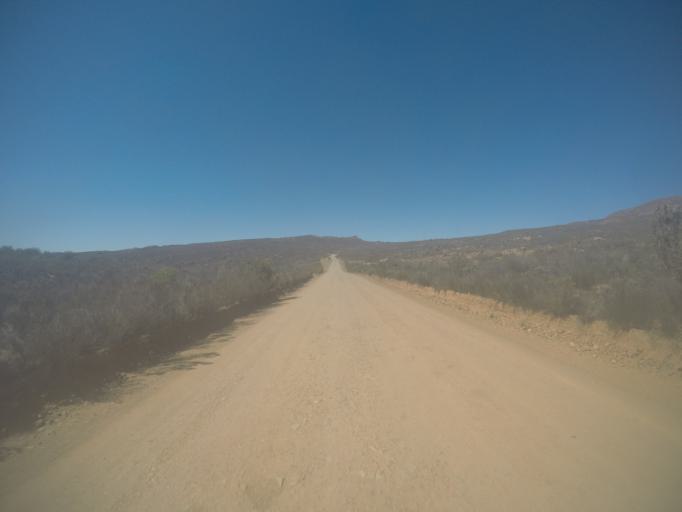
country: ZA
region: Western Cape
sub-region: West Coast District Municipality
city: Clanwilliam
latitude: -32.5024
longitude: 19.2802
